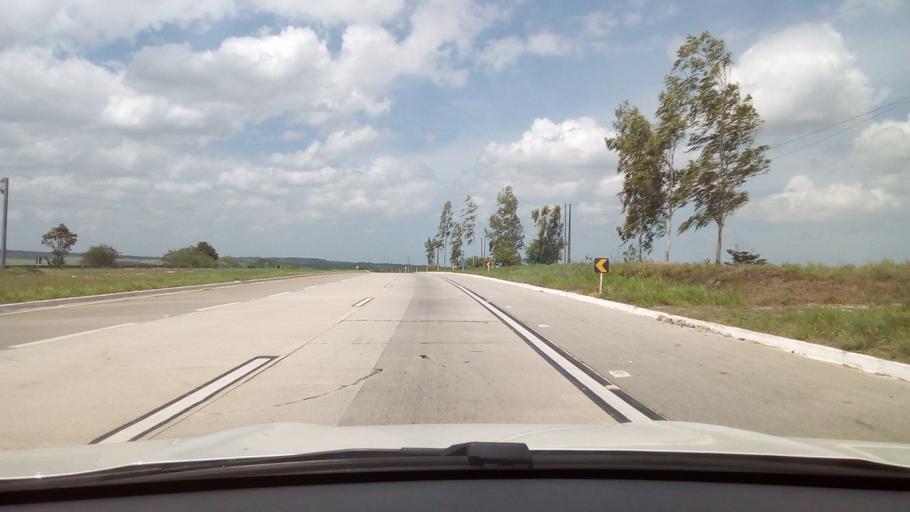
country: BR
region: Paraiba
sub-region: Mamanguape
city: Mamanguape
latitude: -6.7866
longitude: -35.1342
